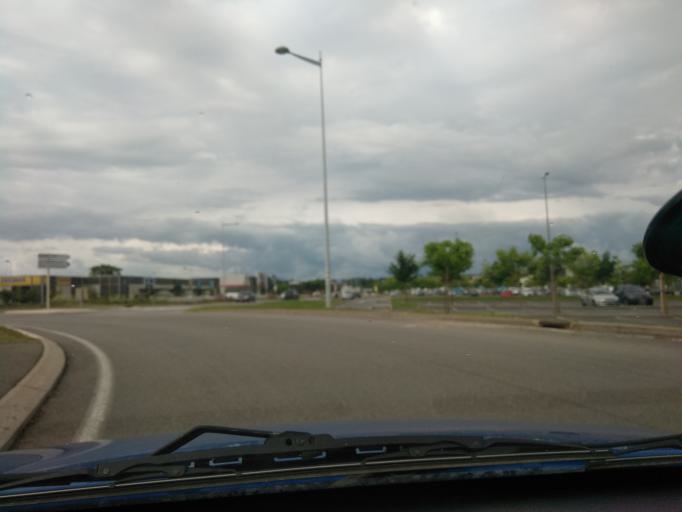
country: FR
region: Midi-Pyrenees
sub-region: Departement de l'Aveyron
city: Sebazac-Concoures
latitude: 44.3952
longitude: 2.6039
